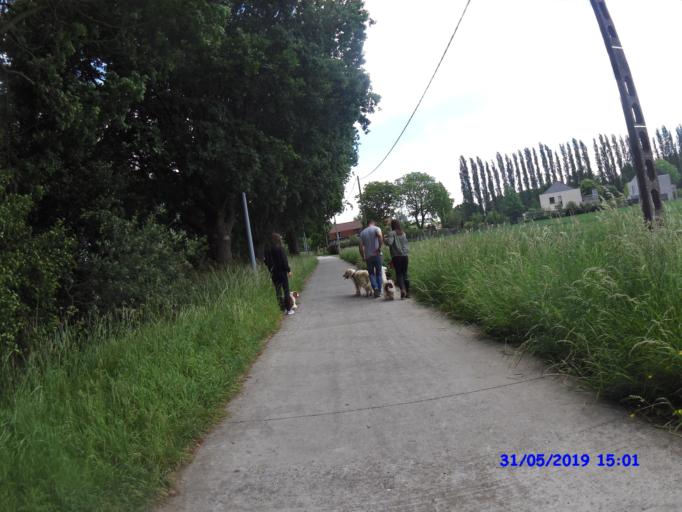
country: FR
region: Nord-Pas-de-Calais
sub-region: Departement du Nord
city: Comines
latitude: 50.7711
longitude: 2.9911
